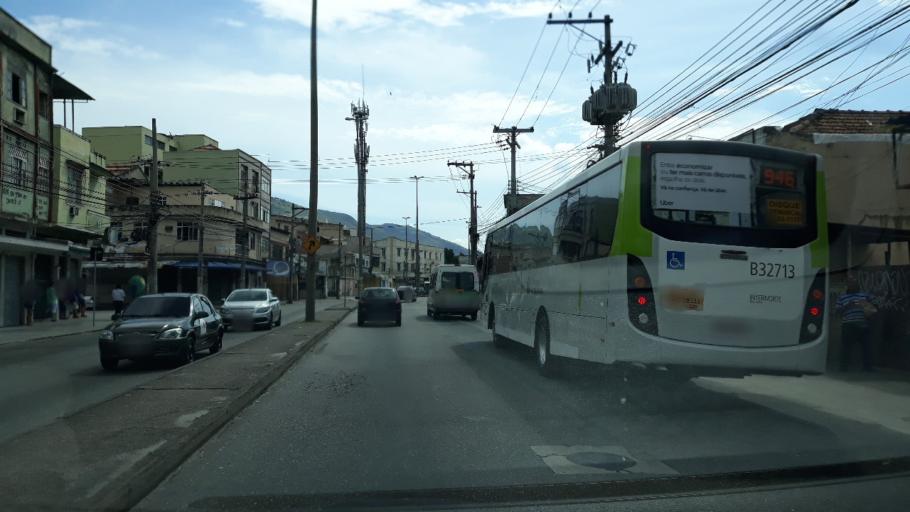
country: BR
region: Rio de Janeiro
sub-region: Rio De Janeiro
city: Rio de Janeiro
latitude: -22.8864
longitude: -43.3029
